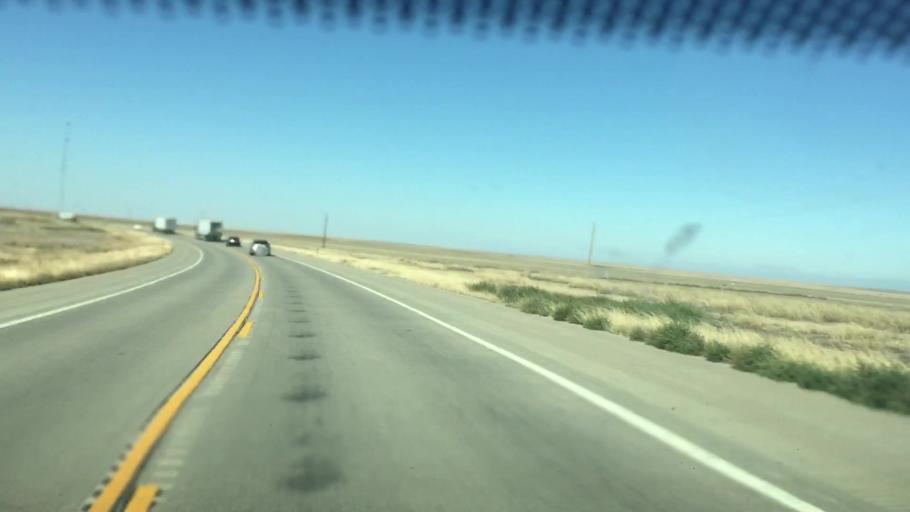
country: US
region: Colorado
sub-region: Prowers County
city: Lamar
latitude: 38.2729
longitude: -102.7205
